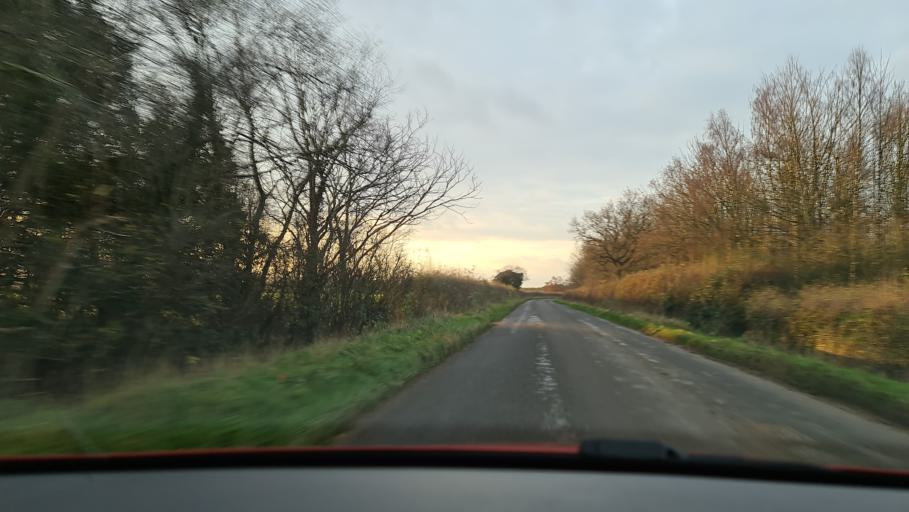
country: GB
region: England
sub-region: Oxfordshire
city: Somerton
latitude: 51.8896
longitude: -1.2734
